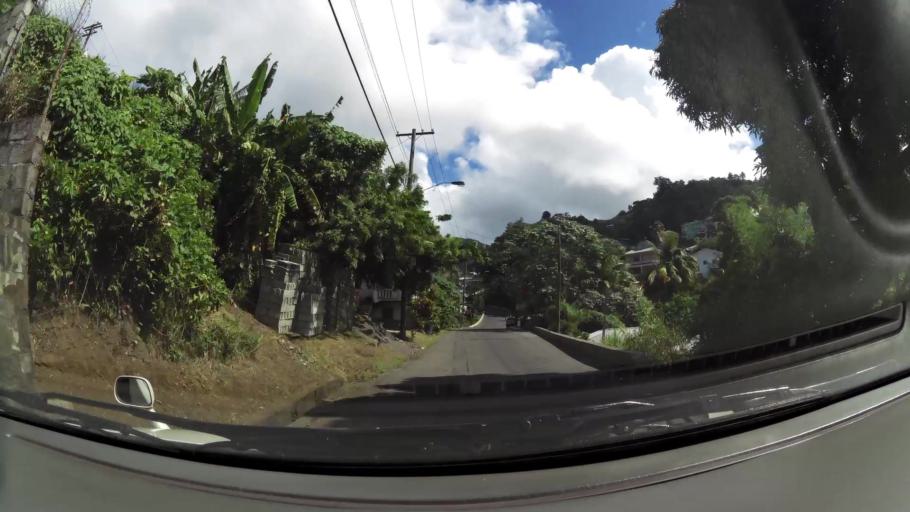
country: VC
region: Saint George
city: Kingstown Park
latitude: 13.1742
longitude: -61.2373
